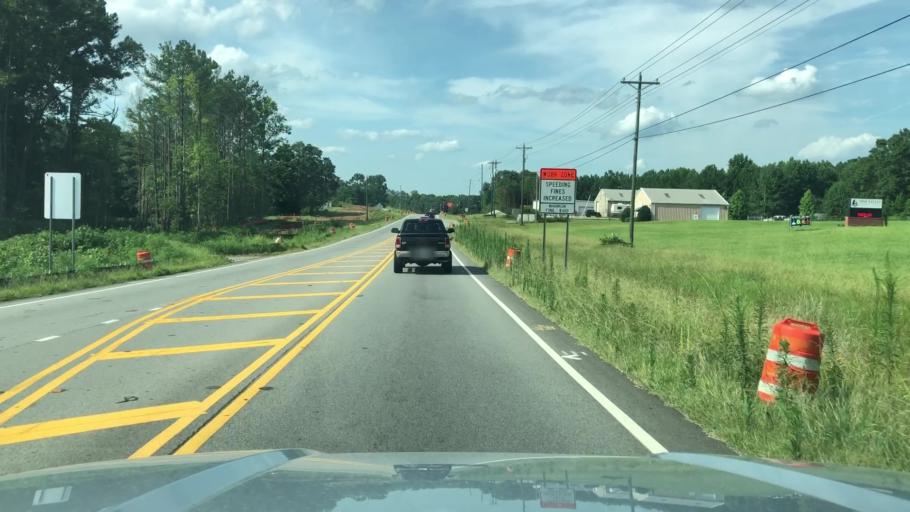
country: US
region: Georgia
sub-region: Paulding County
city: Hiram
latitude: 33.8457
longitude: -84.7572
